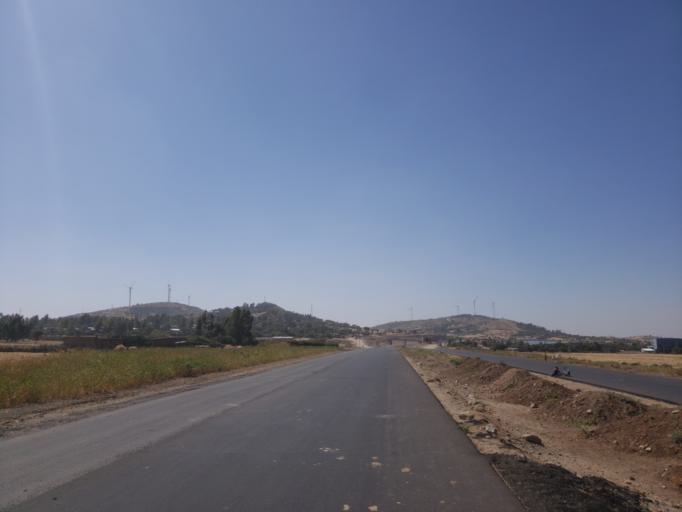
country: ET
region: Oromiya
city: Mojo
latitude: 8.5733
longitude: 39.1689
